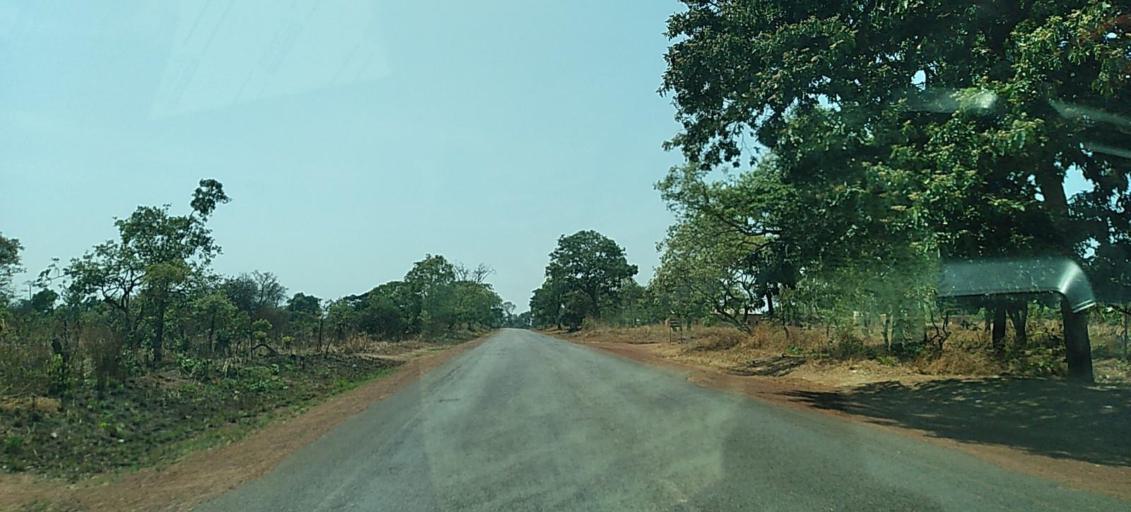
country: ZM
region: North-Western
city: Solwezi
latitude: -12.3209
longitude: 25.8736
